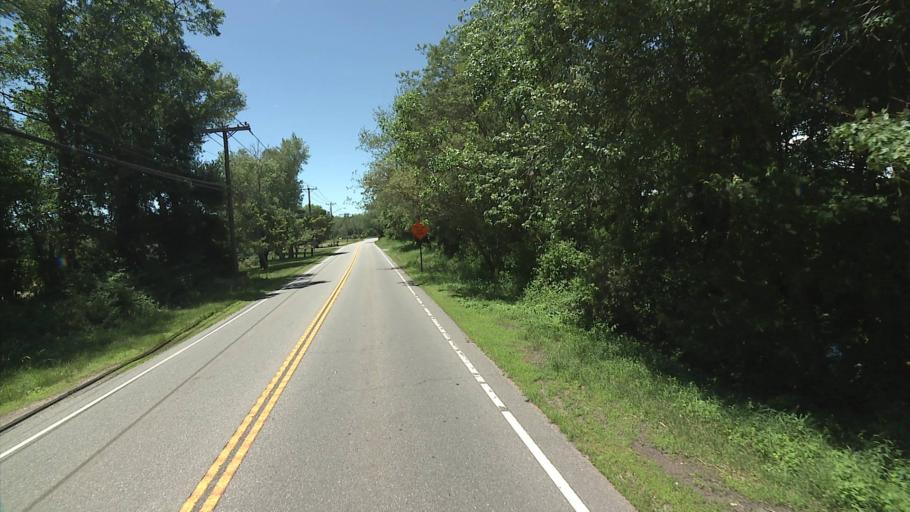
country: US
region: Connecticut
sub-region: New London County
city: Pawcatuck
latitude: 41.3829
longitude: -71.8697
